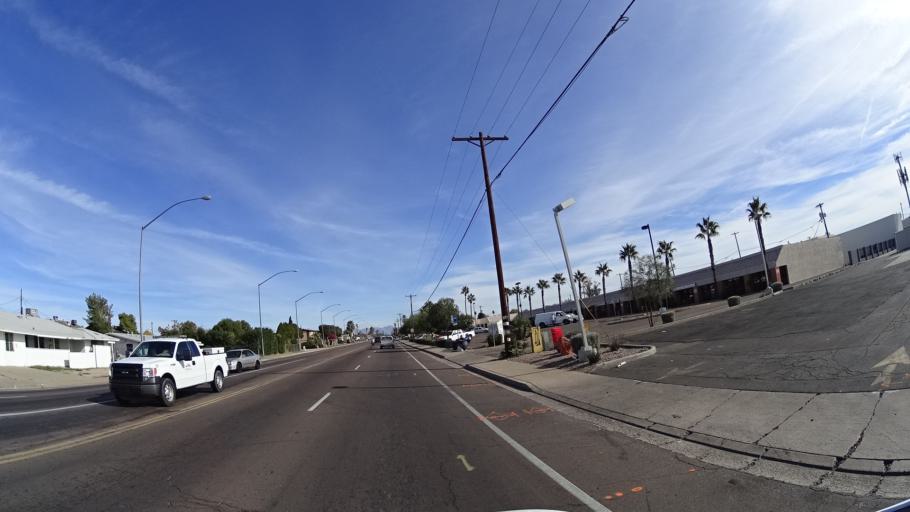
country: US
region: Arizona
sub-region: Maricopa County
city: Mesa
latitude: 33.4078
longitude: -111.8050
